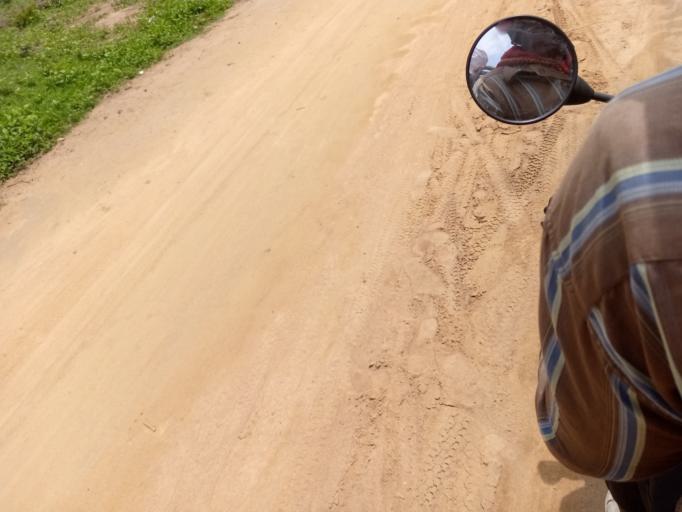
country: SL
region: Western Area
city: Waterloo
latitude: 8.4010
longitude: -12.9952
